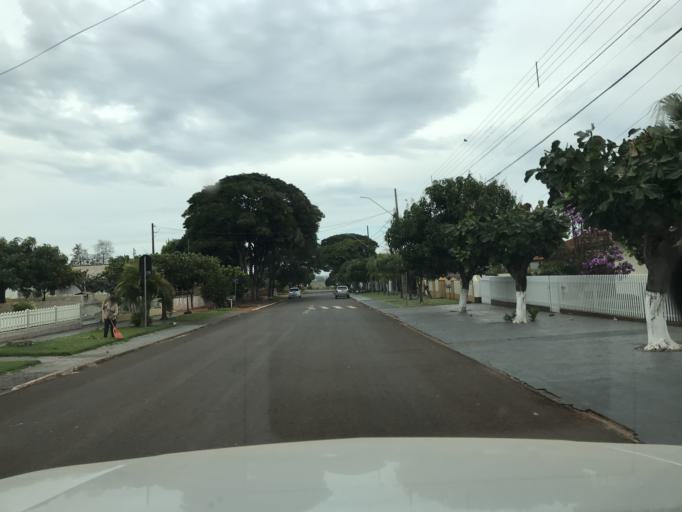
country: BR
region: Parana
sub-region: Marechal Candido Rondon
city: Marechal Candido Rondon
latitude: -24.4672
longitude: -53.9576
